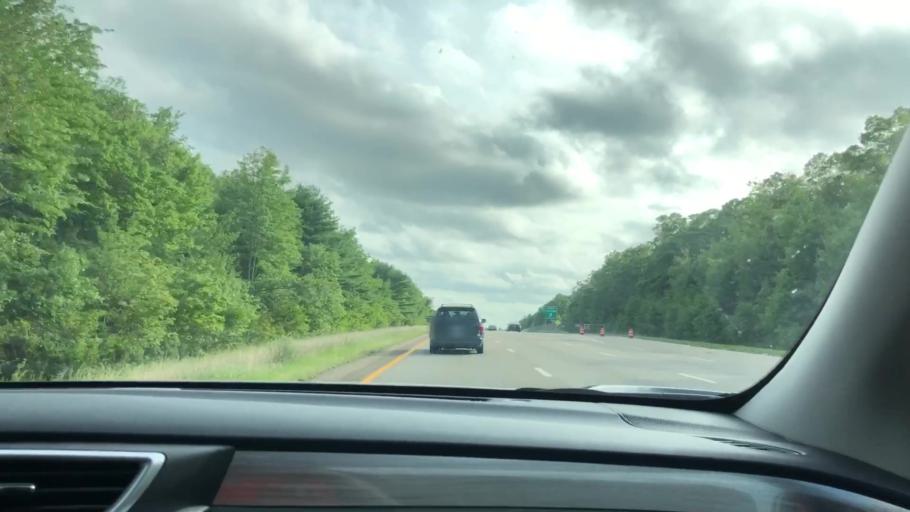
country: US
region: Massachusetts
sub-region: Bristol County
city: North Seekonk
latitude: 41.9201
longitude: -71.3315
